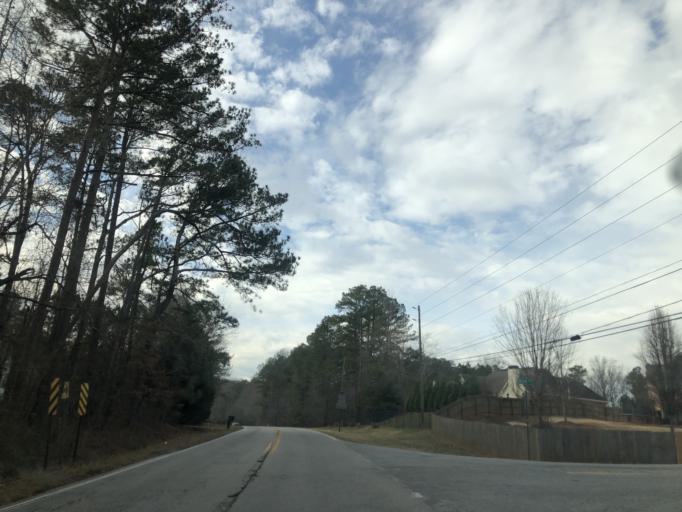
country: US
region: Georgia
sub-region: Henry County
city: Stockbridge
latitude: 33.6074
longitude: -84.2049
